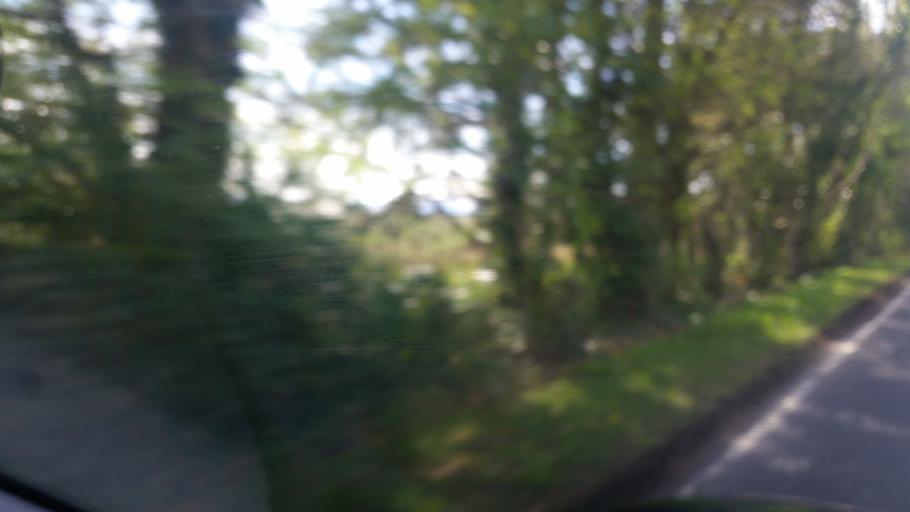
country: IE
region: Ulster
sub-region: County Donegal
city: Ballyshannon
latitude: 54.4734
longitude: -8.0828
